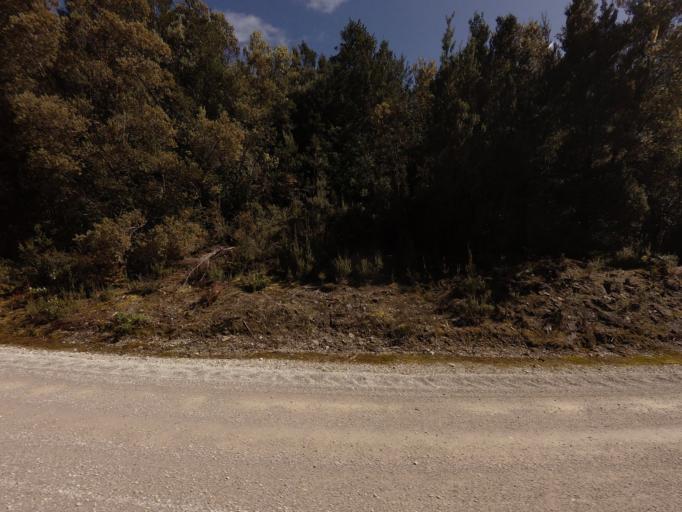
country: AU
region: Tasmania
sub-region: Huon Valley
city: Geeveston
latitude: -42.8346
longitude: 146.3812
